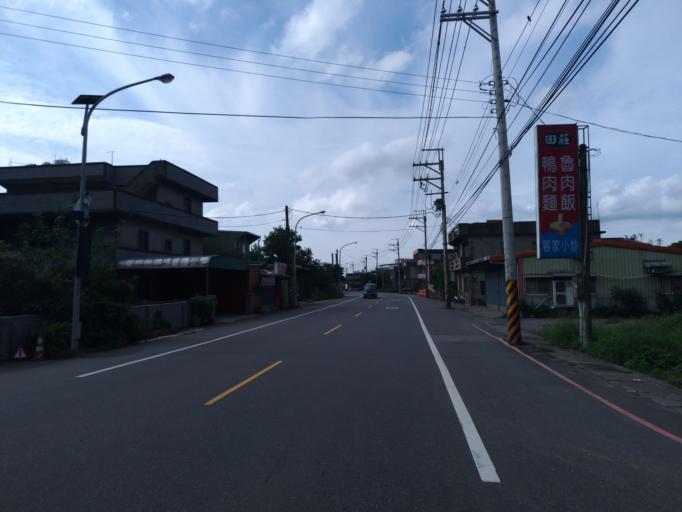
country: TW
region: Taiwan
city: Daxi
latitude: 24.9348
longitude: 121.1698
